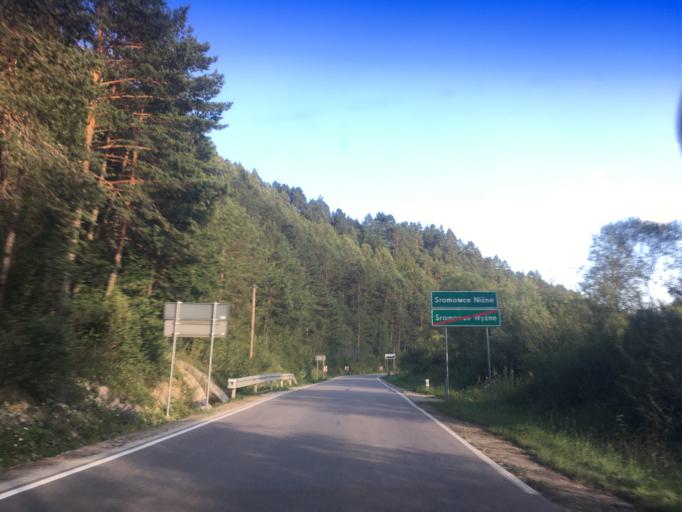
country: PL
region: Lesser Poland Voivodeship
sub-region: Powiat nowotarski
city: Kroscienko nad Dunajcem
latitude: 49.4057
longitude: 20.3802
